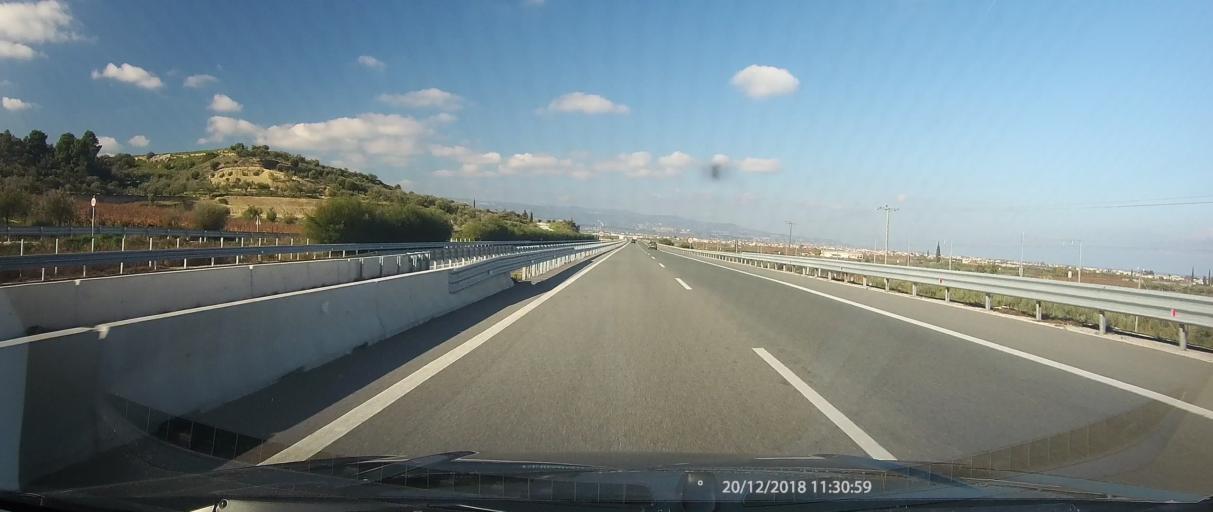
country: GR
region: Peloponnese
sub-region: Nomos Korinthias
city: Assos
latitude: 37.9176
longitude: 22.8255
